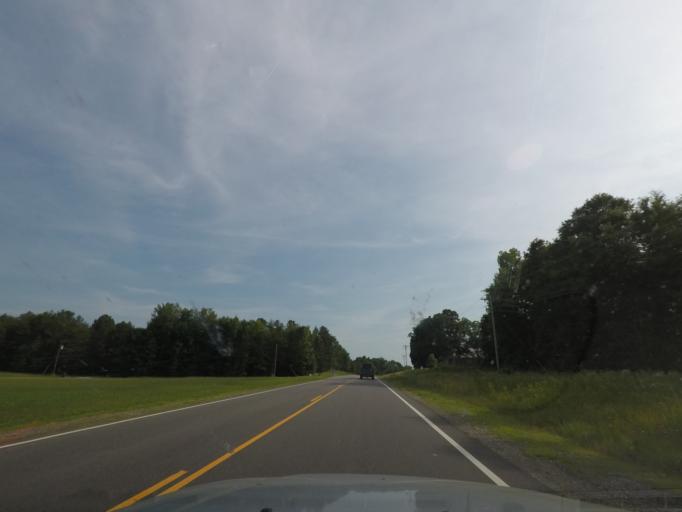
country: US
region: Virginia
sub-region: Mecklenburg County
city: Chase City
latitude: 36.7757
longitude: -78.6195
